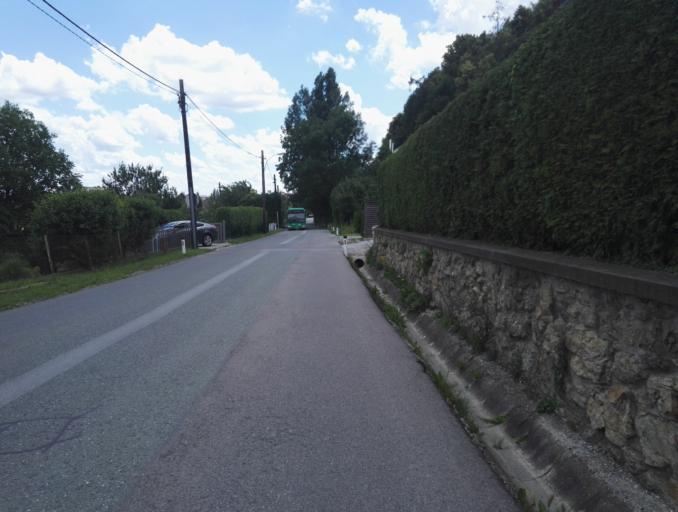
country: AT
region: Styria
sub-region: Graz Stadt
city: Goesting
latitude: 47.0862
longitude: 15.4028
